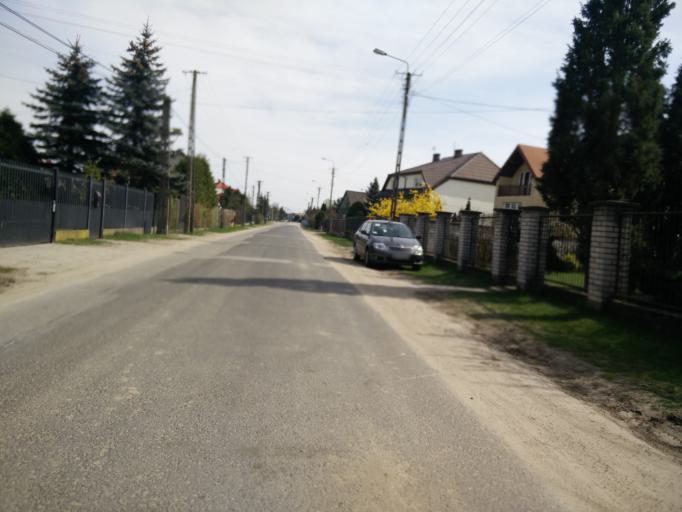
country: PL
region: Masovian Voivodeship
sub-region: Powiat warszawski zachodni
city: Truskaw
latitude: 52.3089
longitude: 20.7647
